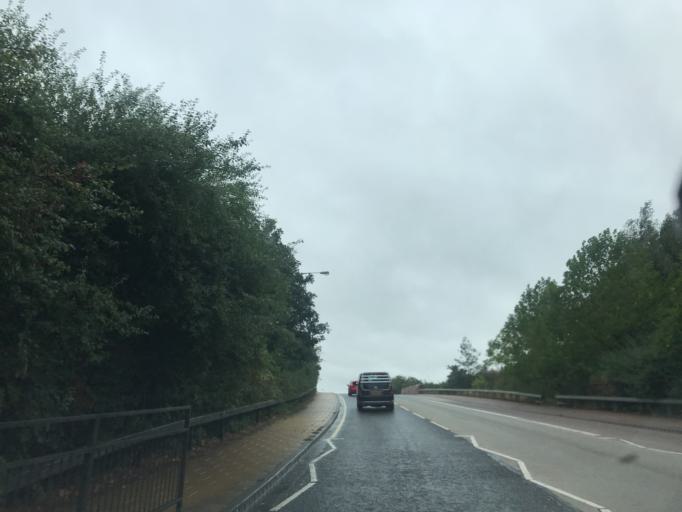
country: GB
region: England
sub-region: Buckinghamshire
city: Aylesbury
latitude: 51.8161
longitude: -0.8220
